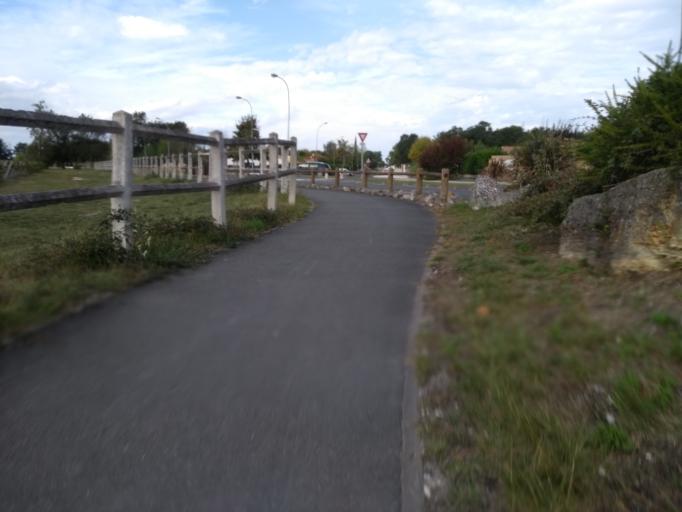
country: FR
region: Aquitaine
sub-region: Departement de la Gironde
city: Canejan
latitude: 44.7633
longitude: -0.6580
